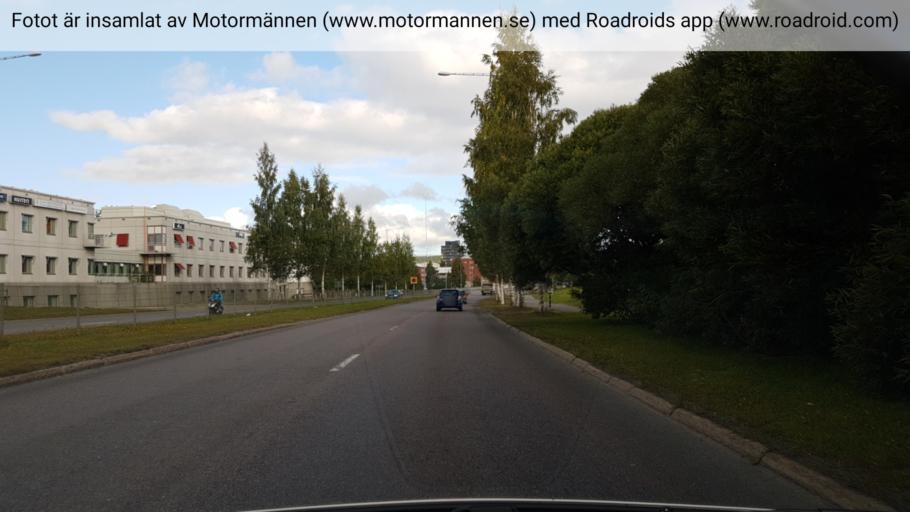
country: SE
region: Vaesterbotten
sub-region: Skelleftea Kommun
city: Skelleftea
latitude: 64.7446
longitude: 20.9600
